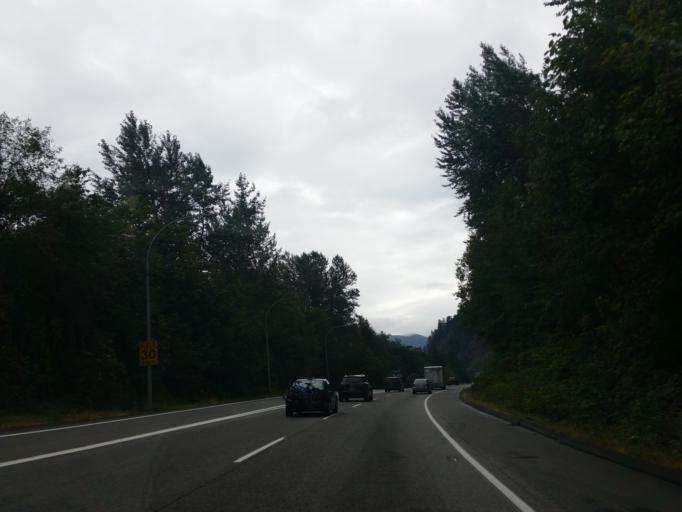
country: CA
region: British Columbia
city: Agassiz
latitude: 49.2544
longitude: -121.6787
